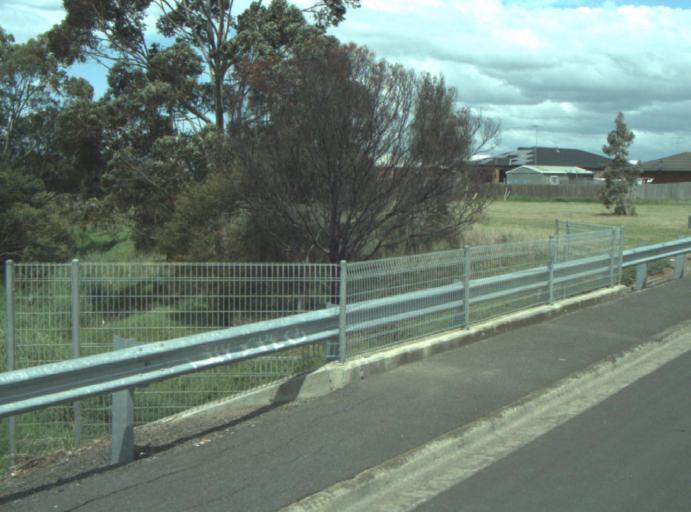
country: AU
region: Victoria
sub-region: Greater Geelong
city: Bell Park
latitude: -38.0925
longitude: 144.3414
